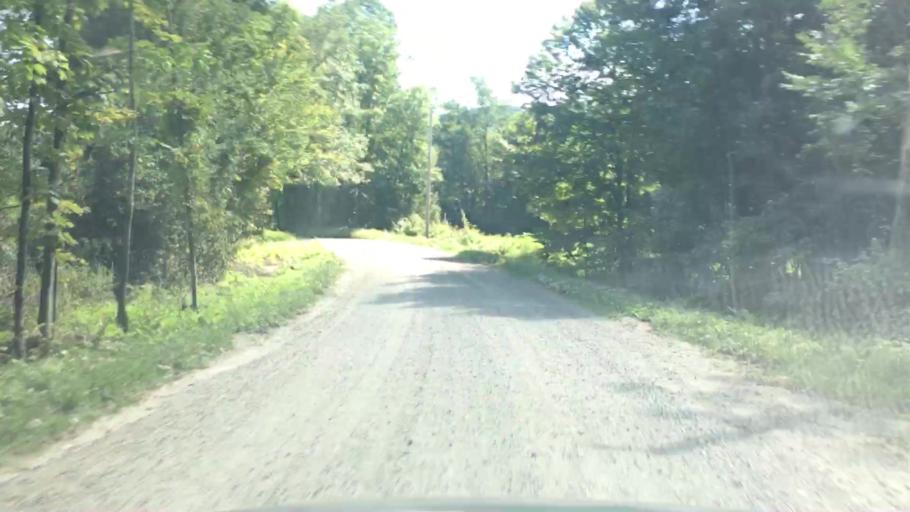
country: US
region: Vermont
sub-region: Windham County
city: West Brattleboro
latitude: 42.7950
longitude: -72.6326
